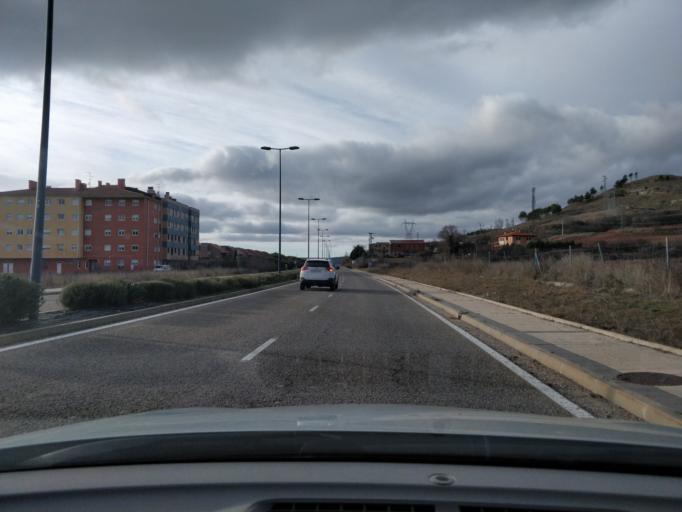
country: ES
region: Castille and Leon
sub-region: Provincia de Burgos
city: Villagonzalo-Pedernales
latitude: 42.3500
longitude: -3.7314
